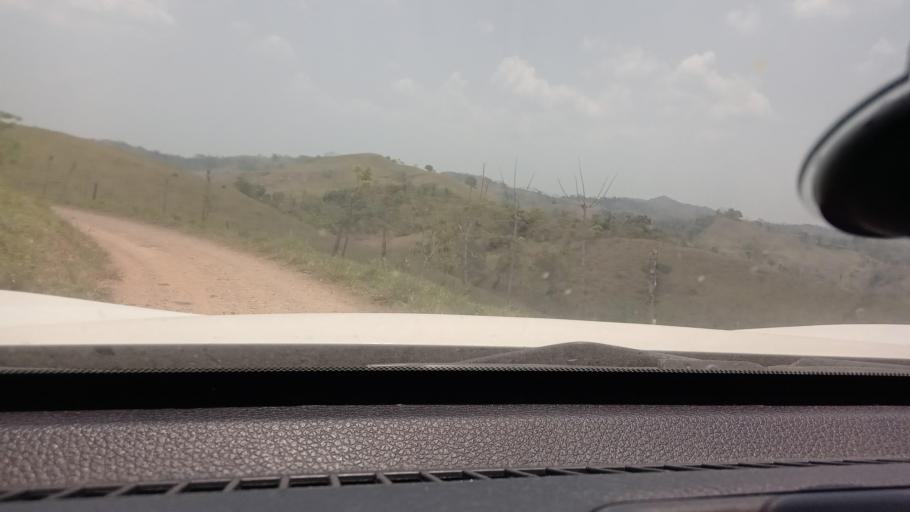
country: MX
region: Tabasco
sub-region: Huimanguillo
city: Francisco Rueda
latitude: 17.4942
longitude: -93.9260
